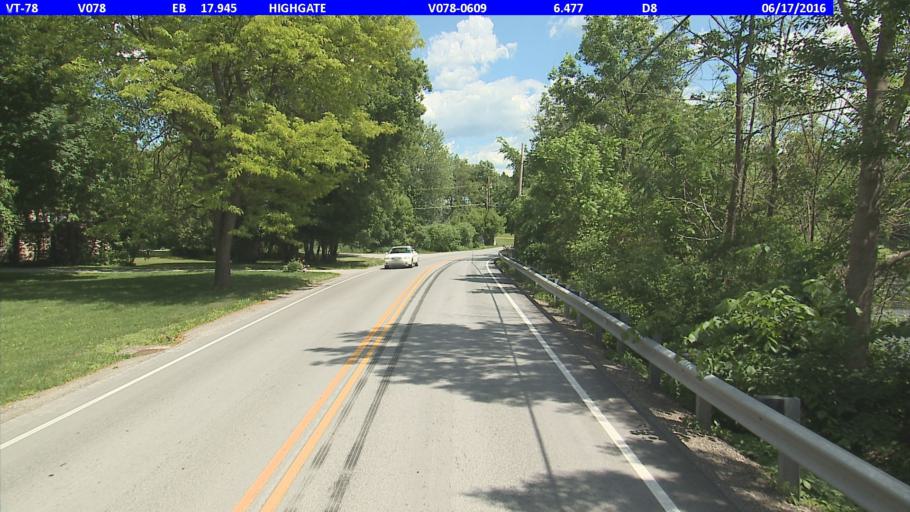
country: US
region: Vermont
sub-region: Franklin County
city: Swanton
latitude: 44.9306
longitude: -72.9874
